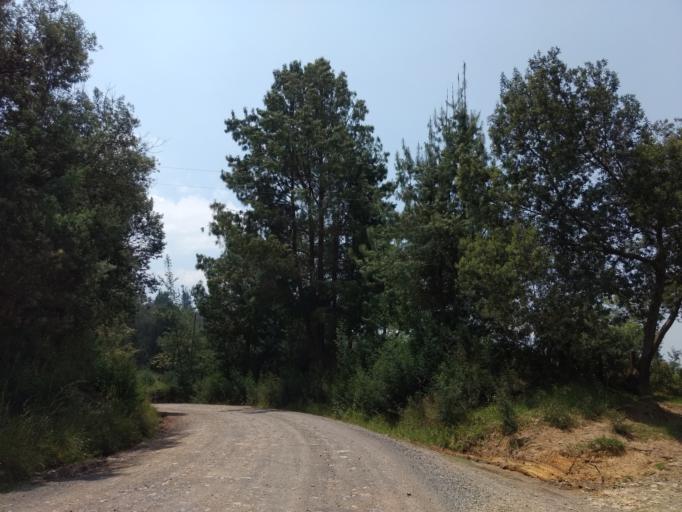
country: CO
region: Boyaca
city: Raquira
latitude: 5.5114
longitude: -73.7183
